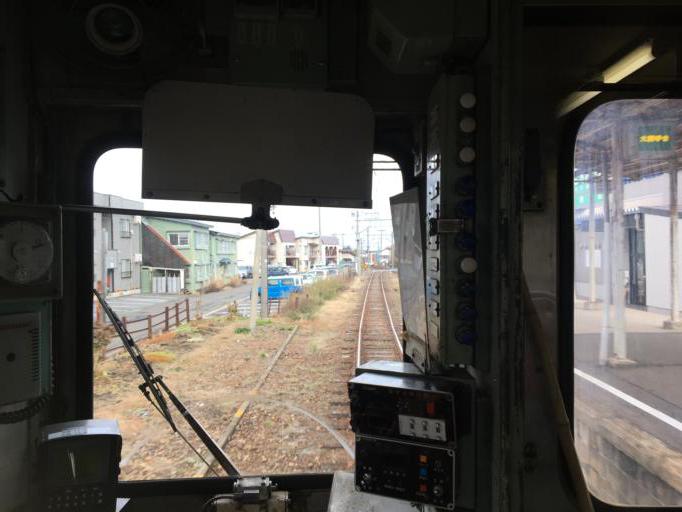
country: JP
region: Aomori
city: Hirosaki
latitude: 40.5836
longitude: 140.4705
